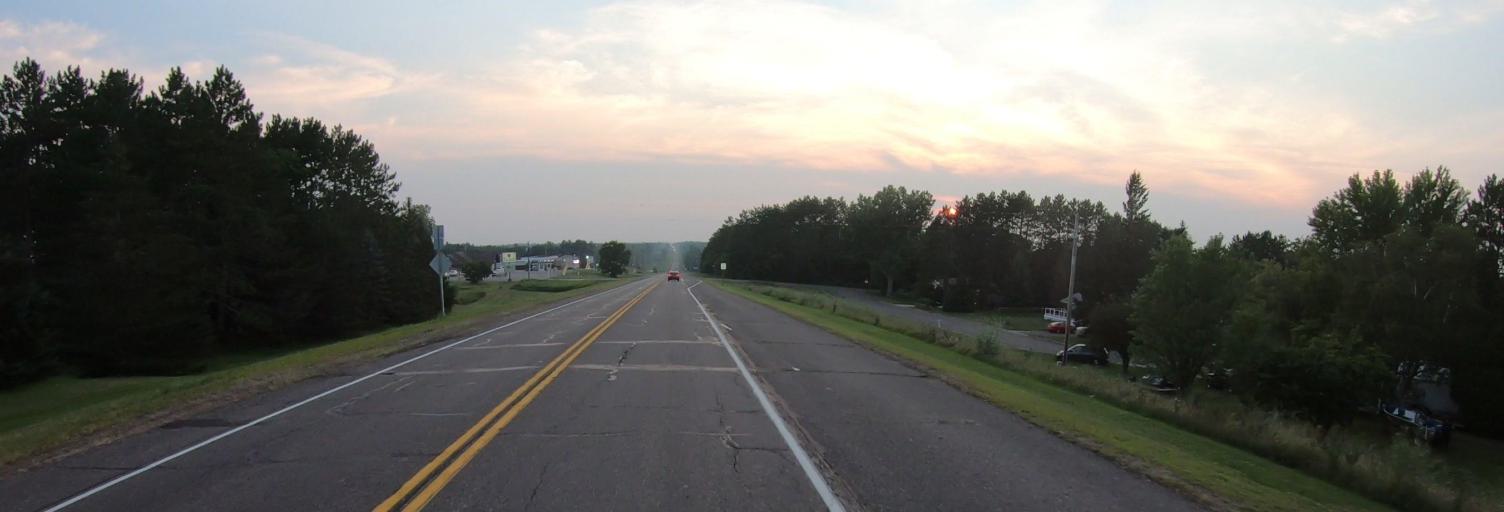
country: US
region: Wisconsin
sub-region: Burnett County
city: Grantsburg
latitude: 45.7730
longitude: -92.6932
